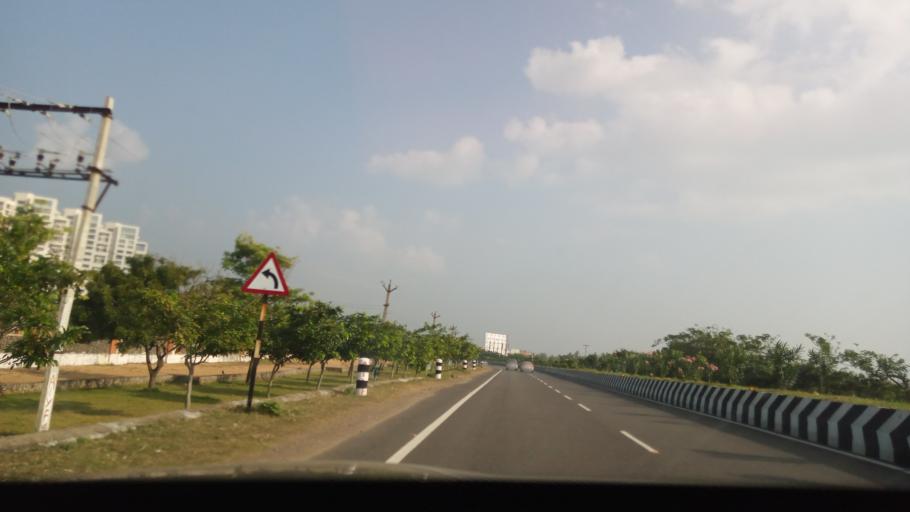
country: IN
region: Tamil Nadu
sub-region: Kancheepuram
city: Injambakkam
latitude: 12.7712
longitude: 80.2483
